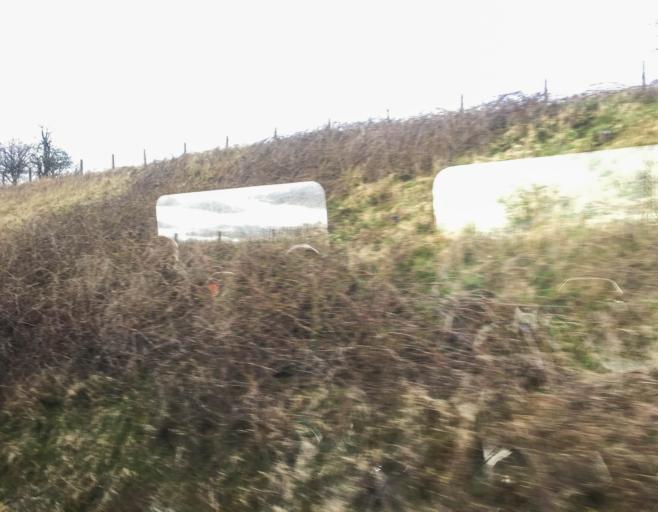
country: GB
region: Scotland
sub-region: North Lanarkshire
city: Wishaw
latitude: 55.7619
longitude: -3.9069
